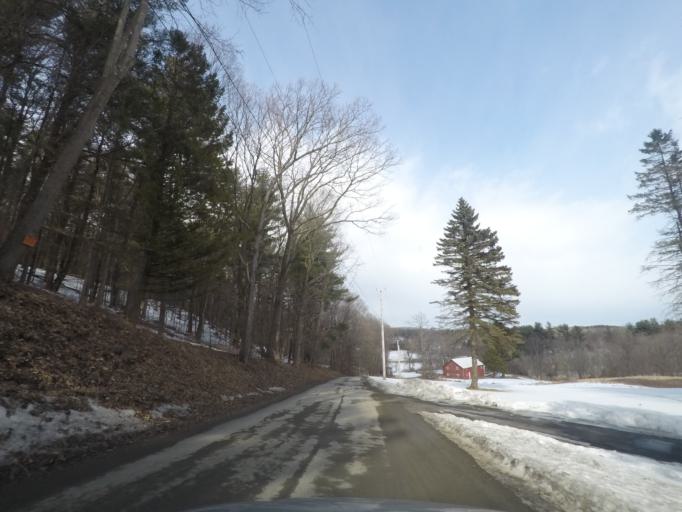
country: US
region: New York
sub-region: Saratoga County
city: Waterford
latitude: 42.7864
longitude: -73.5868
